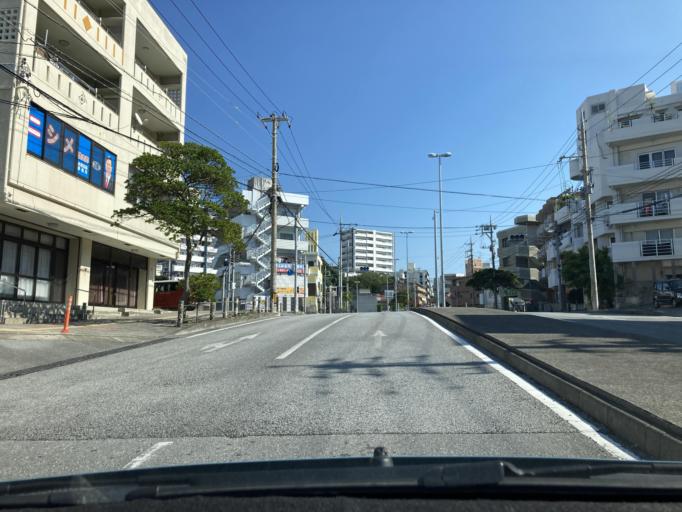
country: JP
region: Okinawa
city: Naha-shi
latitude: 26.2040
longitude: 127.7057
